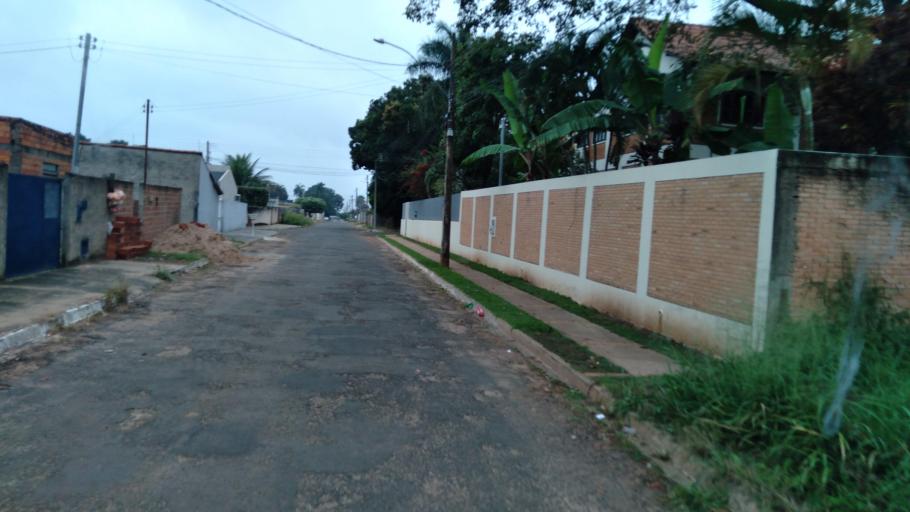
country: BR
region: Goias
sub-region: Mineiros
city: Mineiros
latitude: -17.5803
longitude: -52.5475
